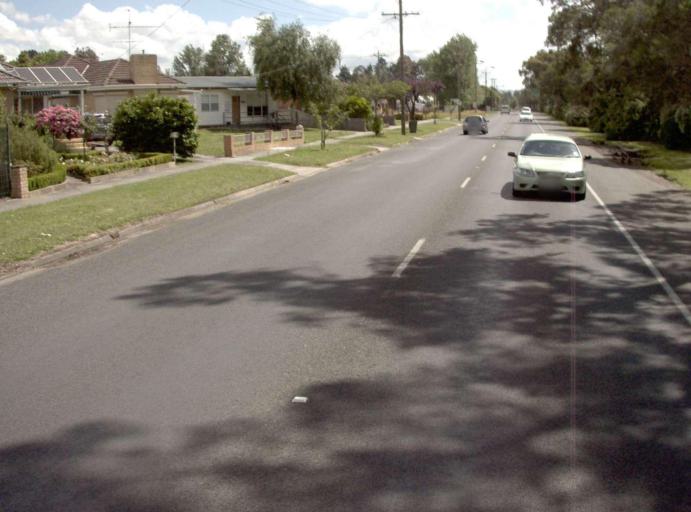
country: AU
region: Victoria
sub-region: Latrobe
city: Moe
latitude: -38.1824
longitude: 146.2429
